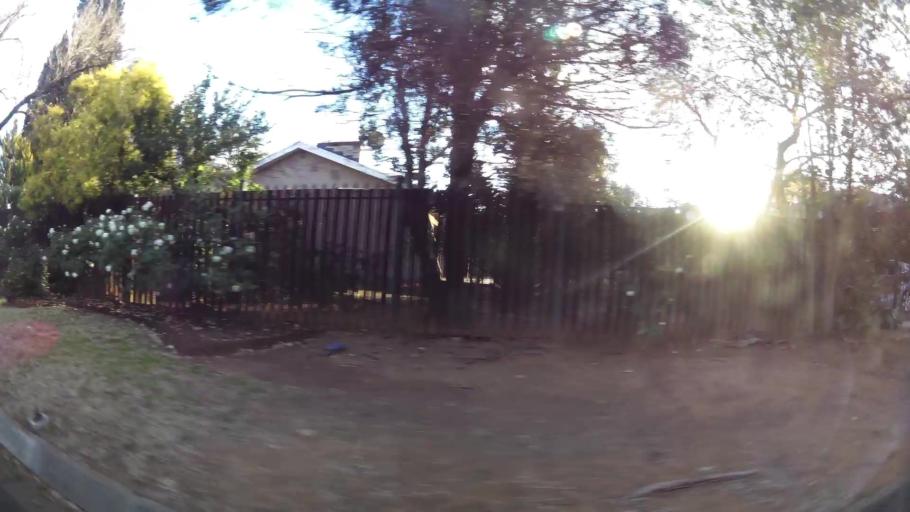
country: ZA
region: Orange Free State
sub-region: Mangaung Metropolitan Municipality
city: Bloemfontein
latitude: -29.1365
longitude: 26.1884
